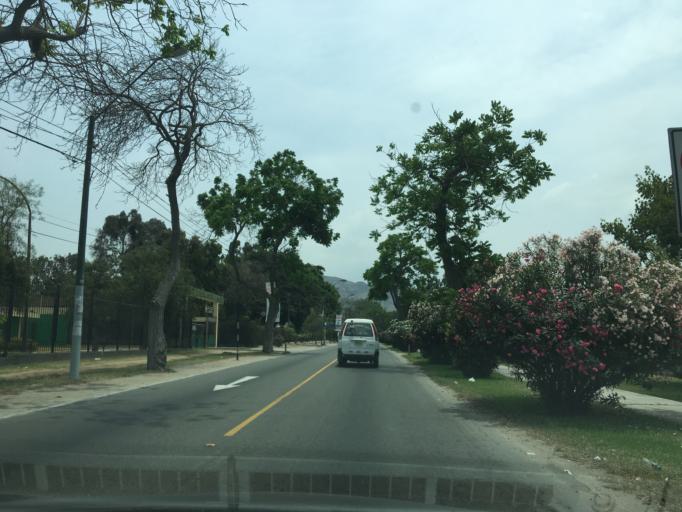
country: PE
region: Lima
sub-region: Lima
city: La Molina
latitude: -12.0794
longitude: -76.9501
